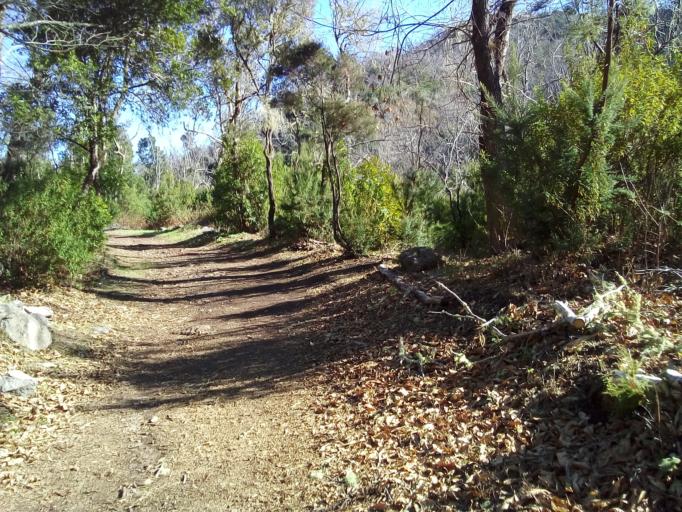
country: ES
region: Canary Islands
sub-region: Provincia de Santa Cruz de Tenerife
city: Vallehermosa
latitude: 28.1223
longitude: -17.2613
